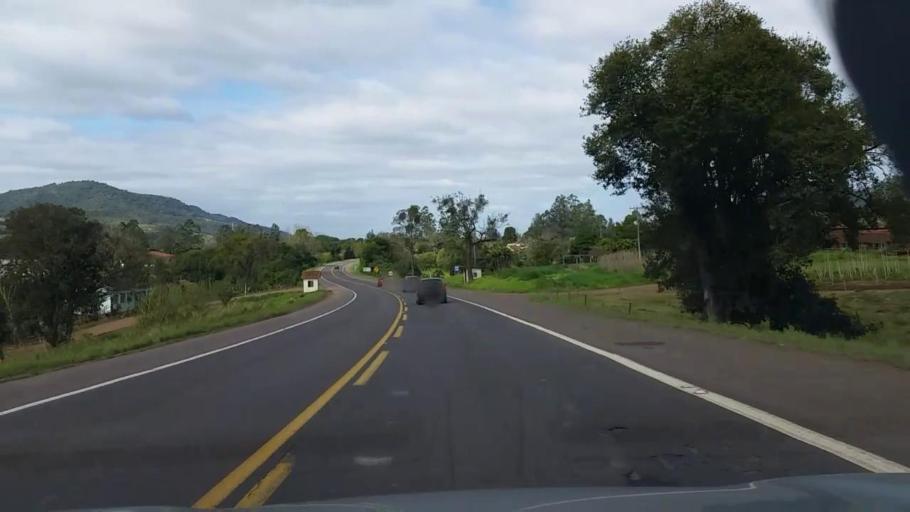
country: BR
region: Rio Grande do Sul
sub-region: Arroio Do Meio
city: Arroio do Meio
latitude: -29.3412
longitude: -52.0774
